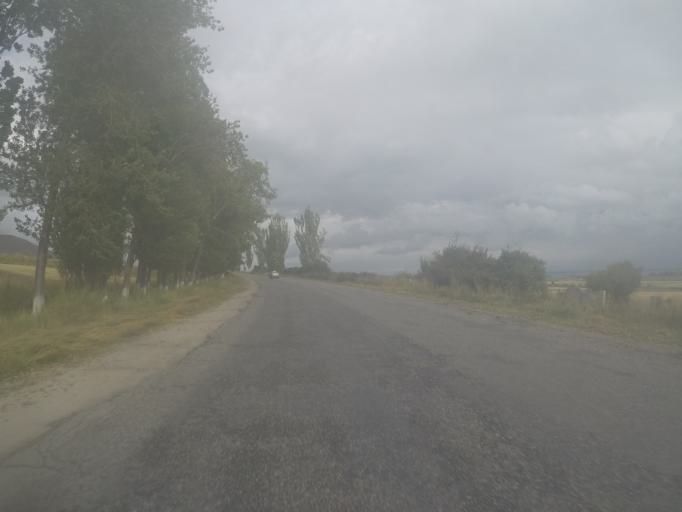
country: KG
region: Ysyk-Koel
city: Tyup
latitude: 42.7418
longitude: 78.0587
